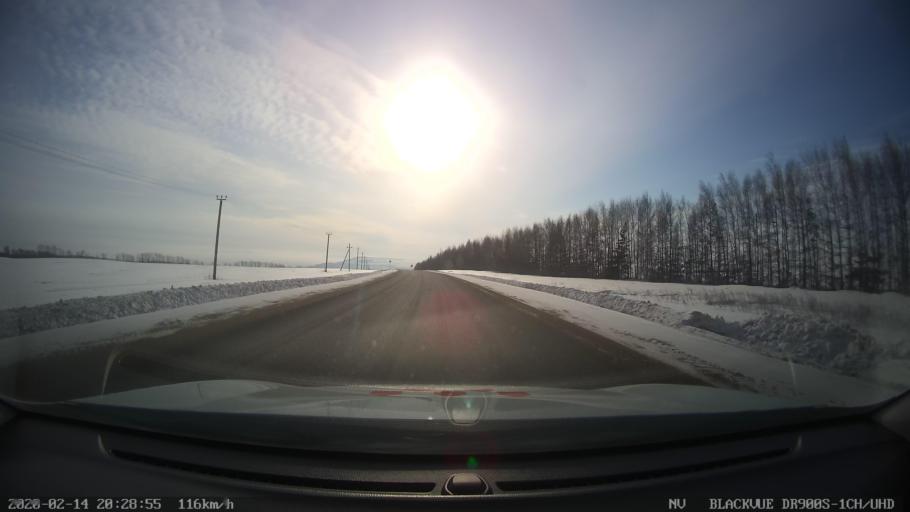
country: RU
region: Tatarstan
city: Stolbishchi
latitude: 55.4560
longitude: 48.9781
